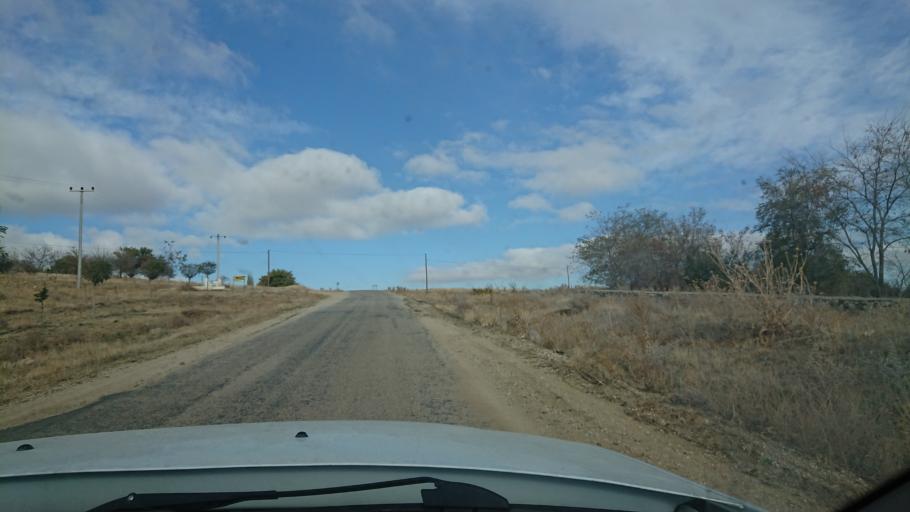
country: TR
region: Aksaray
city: Agacoren
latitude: 38.8133
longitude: 33.9833
